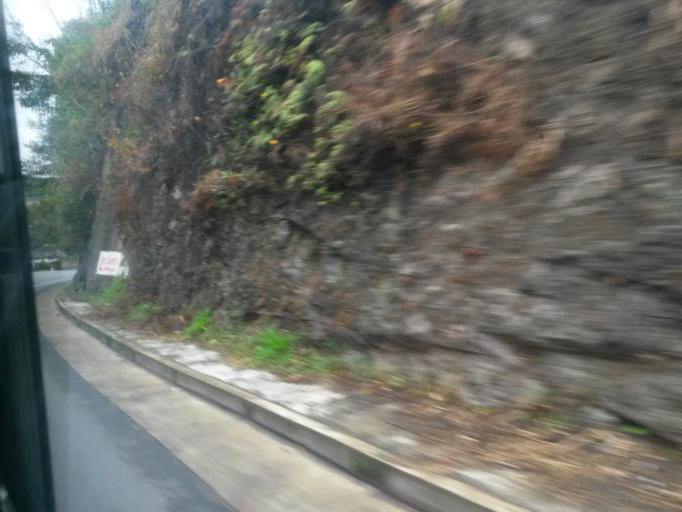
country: CO
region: Cauca
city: Popayan
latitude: 2.4243
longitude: -76.6245
